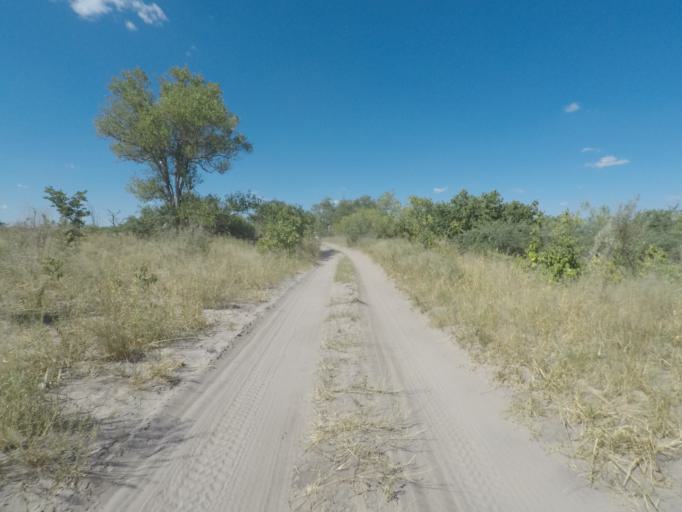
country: BW
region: North West
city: Maun
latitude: -19.4265
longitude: 23.6329
